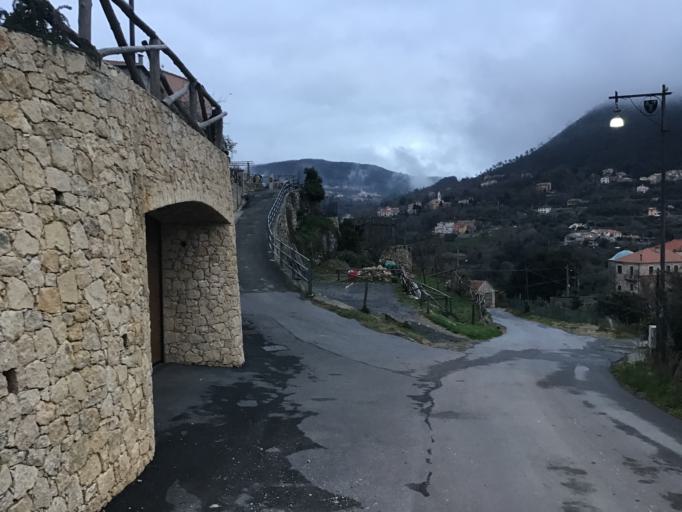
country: IT
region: Liguria
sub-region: Provincia di Savona
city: Vezzi Portio
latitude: 44.2157
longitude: 8.3526
